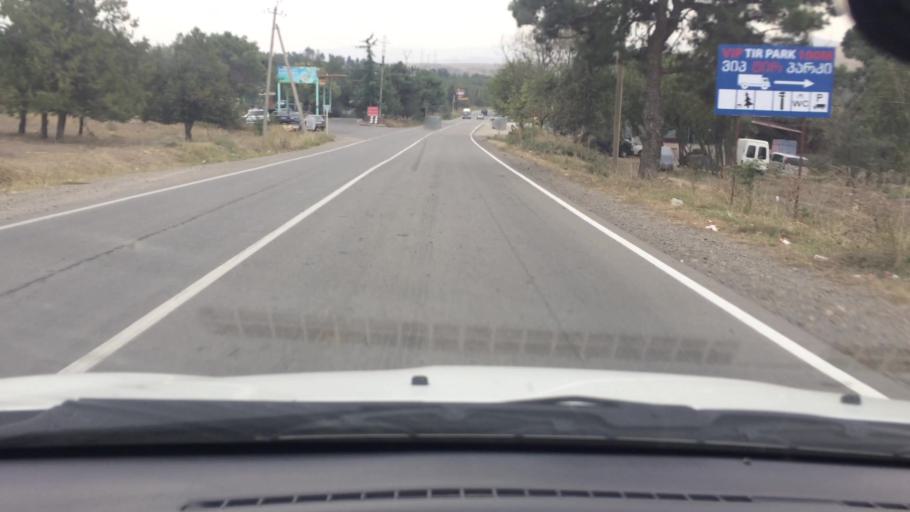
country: GE
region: Kvemo Kartli
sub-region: Gardabani
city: Gardabani
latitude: 41.3422
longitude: 45.0686
